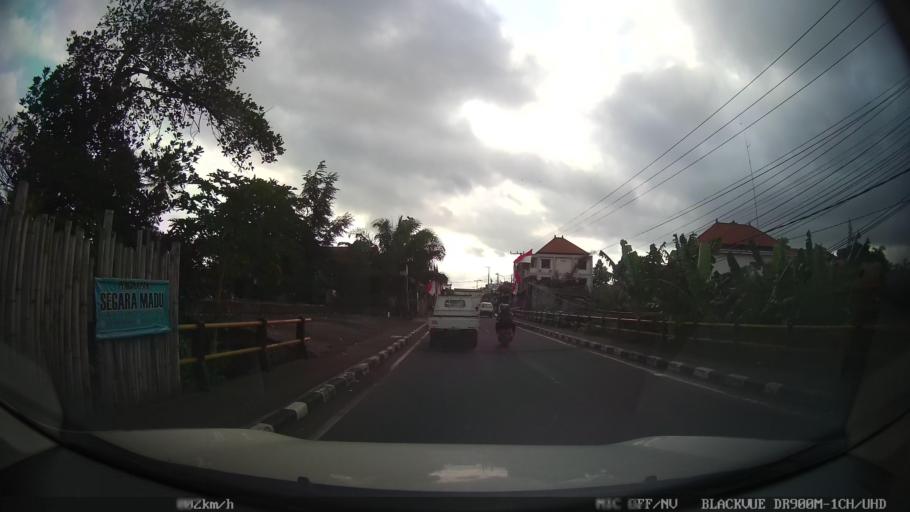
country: ID
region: Bali
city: Banjar Mambalkajanan
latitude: -8.5500
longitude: 115.2234
